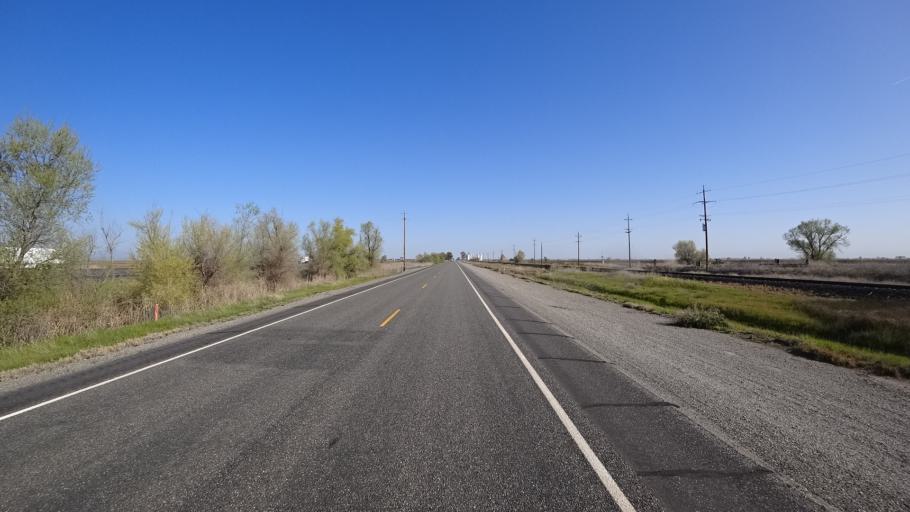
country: US
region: California
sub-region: Glenn County
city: Willows
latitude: 39.4502
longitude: -122.1929
